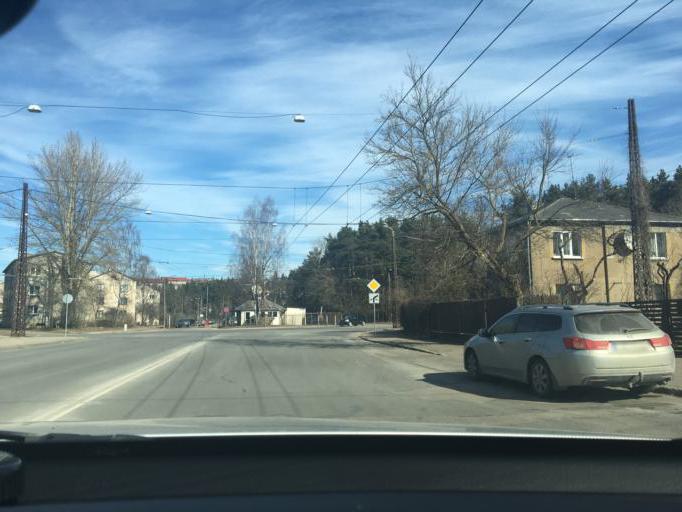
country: LV
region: Riga
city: Jaunciems
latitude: 56.9652
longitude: 24.1954
